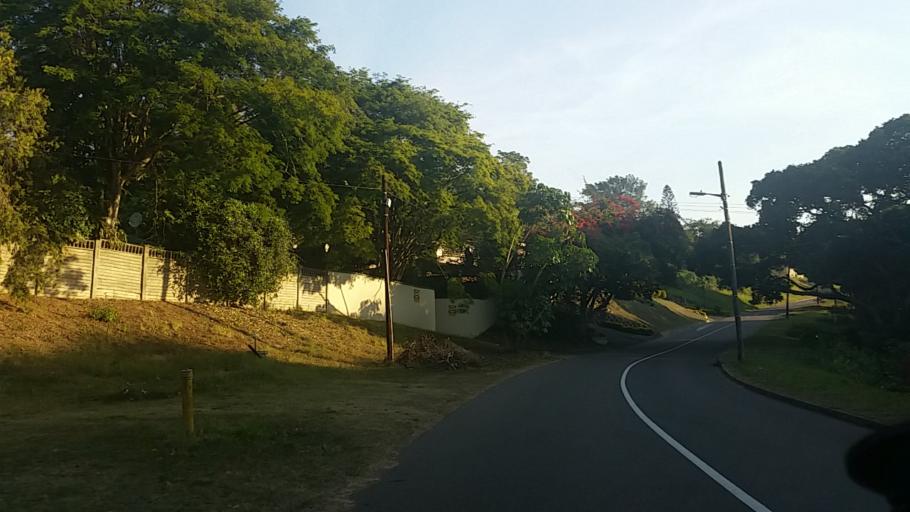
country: ZA
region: KwaZulu-Natal
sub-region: eThekwini Metropolitan Municipality
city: Berea
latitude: -29.8479
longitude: 30.9153
